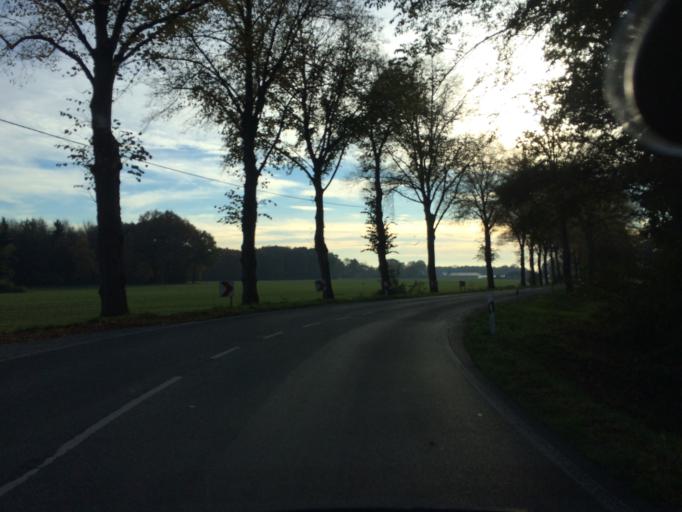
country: DE
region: North Rhine-Westphalia
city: Marl
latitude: 51.6942
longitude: 7.0479
